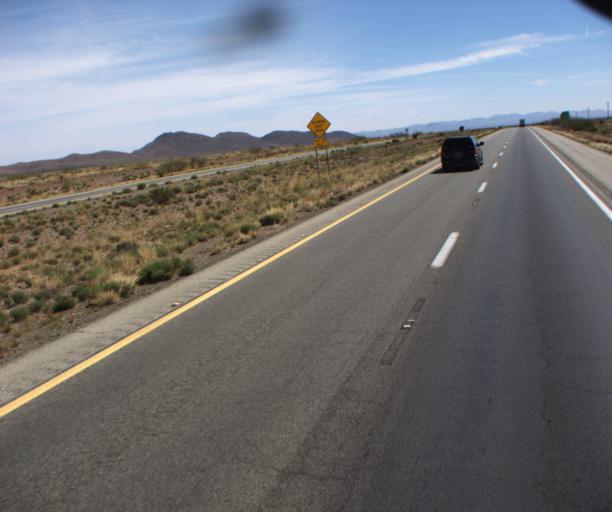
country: US
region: Arizona
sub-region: Cochise County
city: Willcox
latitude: 32.3625
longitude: -109.6376
